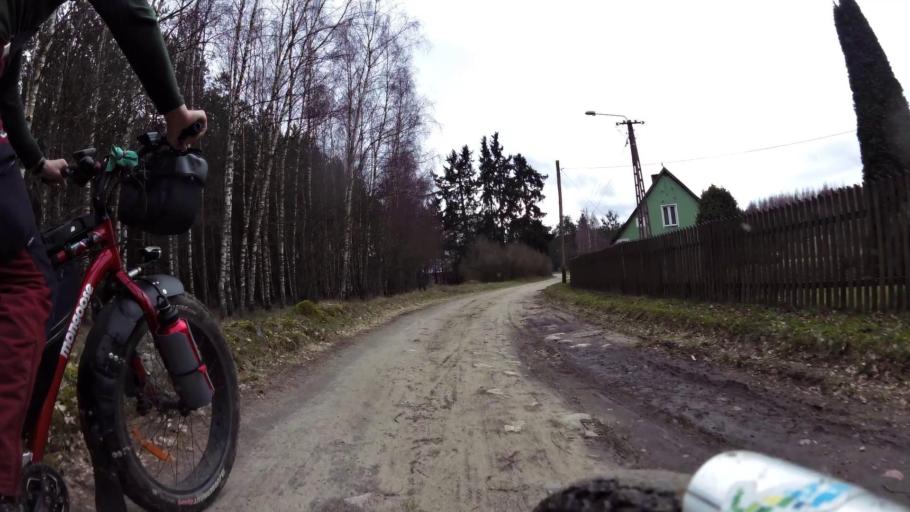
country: PL
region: Pomeranian Voivodeship
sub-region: Powiat bytowski
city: Kolczyglowy
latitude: 54.1549
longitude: 17.1870
